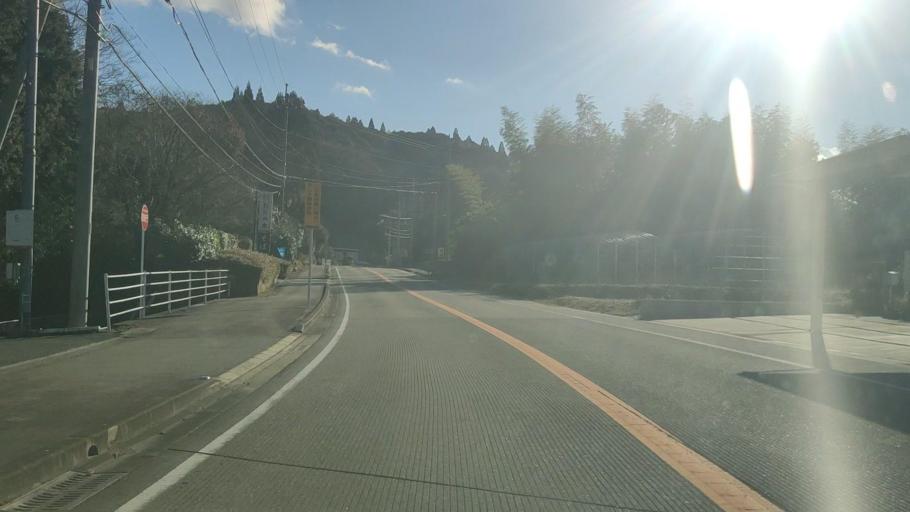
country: JP
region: Fukuoka
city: Maebaru-chuo
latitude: 33.4438
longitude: 130.2690
